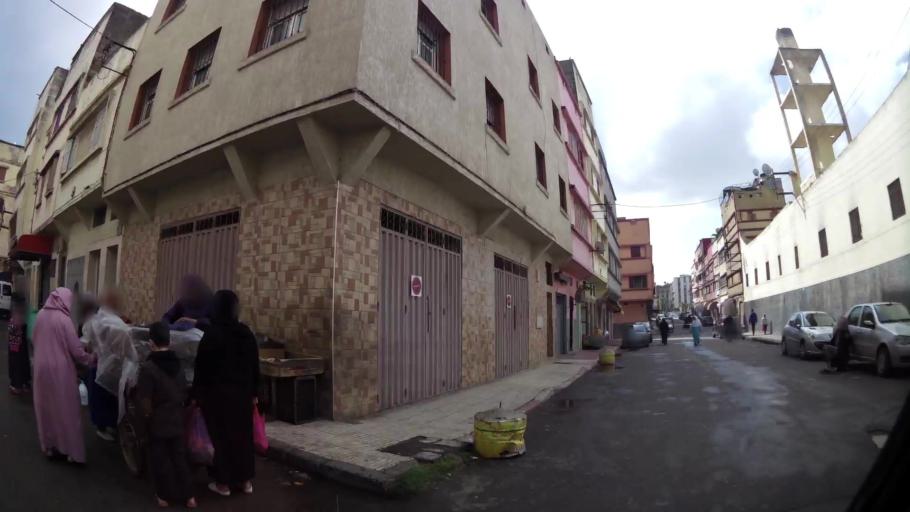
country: MA
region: Grand Casablanca
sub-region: Casablanca
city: Casablanca
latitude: 33.5674
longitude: -7.5889
